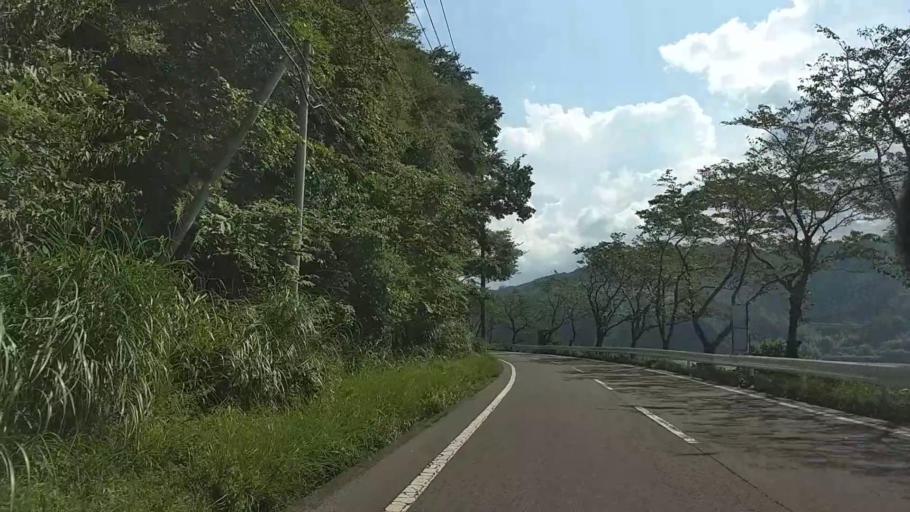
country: JP
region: Shizuoka
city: Fujinomiya
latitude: 35.3970
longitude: 138.4495
